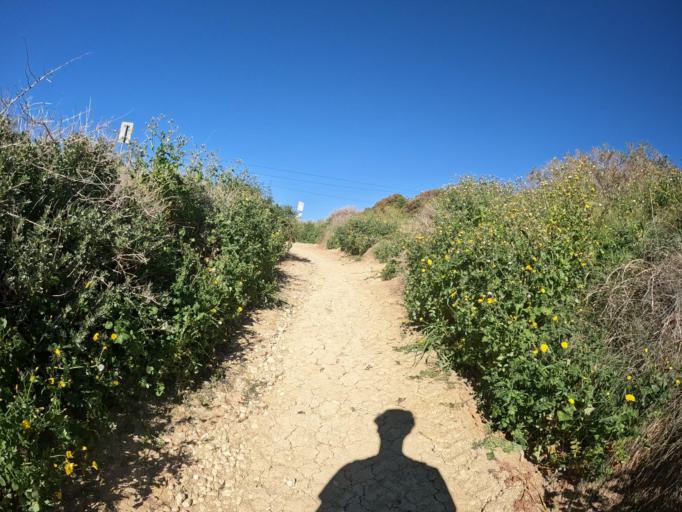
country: MT
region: L-Imgarr
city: Imgarr
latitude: 35.9306
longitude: 14.3464
